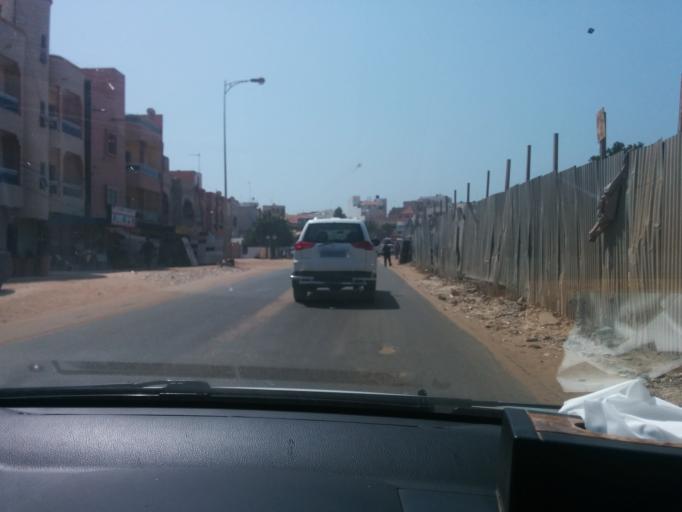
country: SN
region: Dakar
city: Grand Dakar
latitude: 14.7531
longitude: -17.4544
